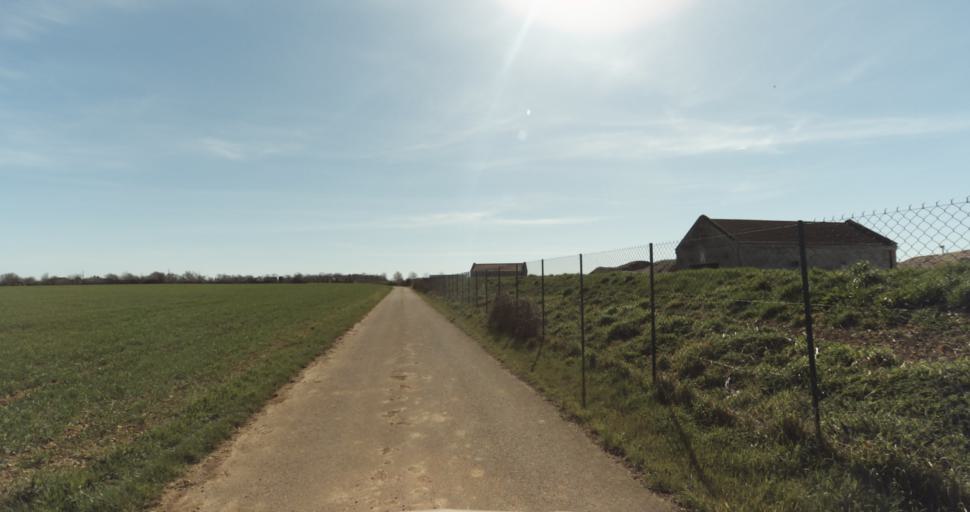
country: FR
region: Lower Normandy
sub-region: Departement du Calvados
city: Saint-Pierre-sur-Dives
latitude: 49.0482
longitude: -0.0460
